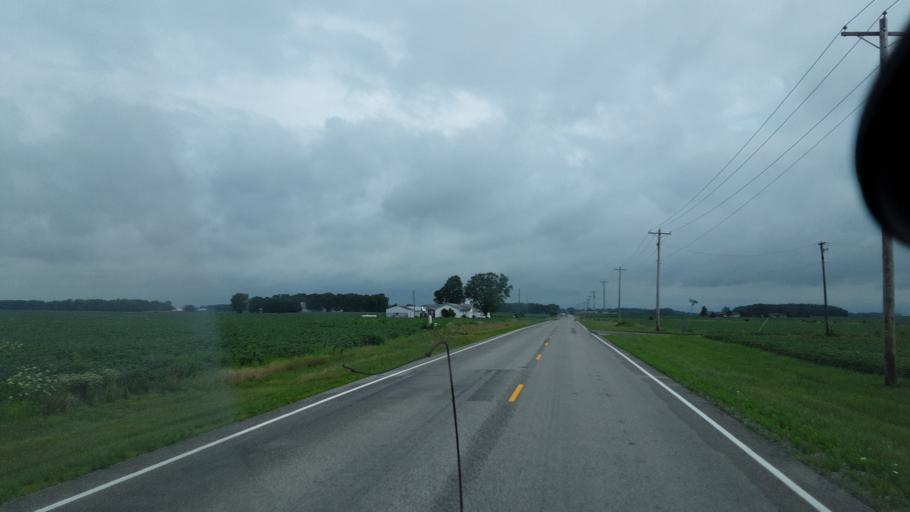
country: US
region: Indiana
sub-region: Allen County
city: Monroeville
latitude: 40.9421
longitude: -84.8620
